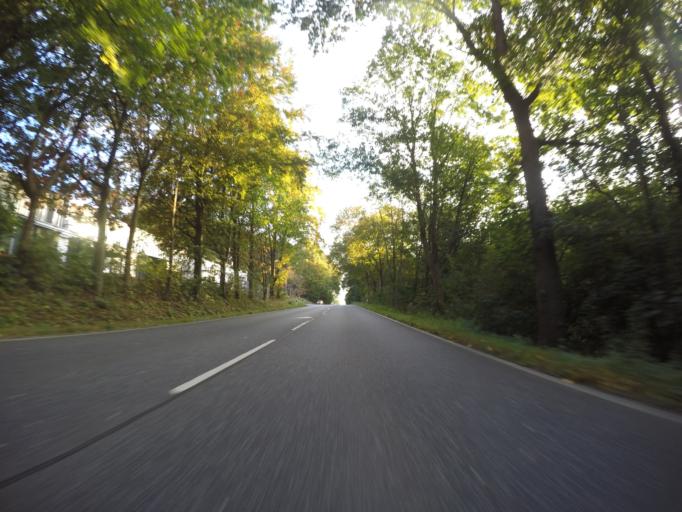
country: DE
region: Rheinland-Pfalz
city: Kleinmaischeid
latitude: 50.5177
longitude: 7.6077
